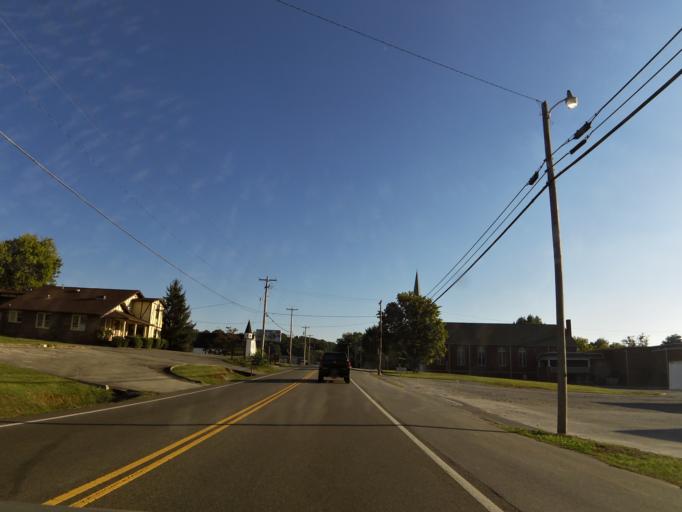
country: US
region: Tennessee
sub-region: Blount County
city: Eagleton Village
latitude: 35.7866
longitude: -83.9472
